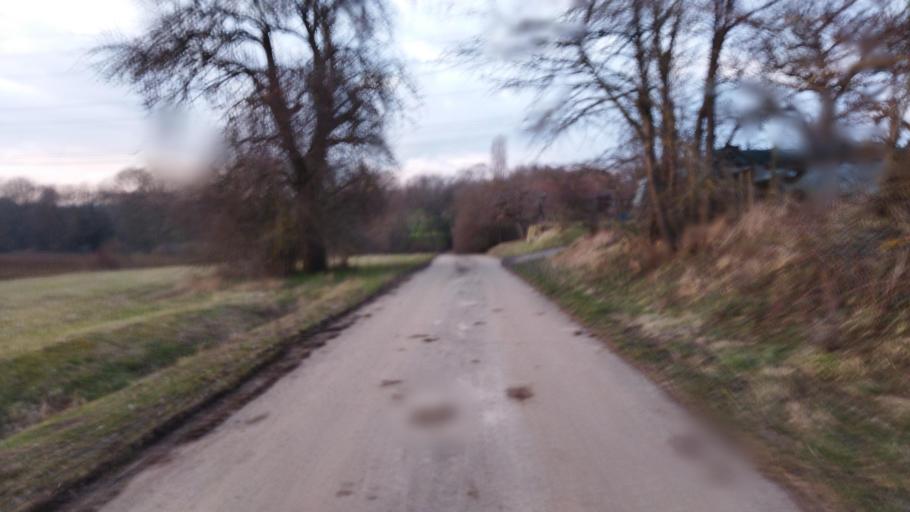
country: DE
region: Baden-Wuerttemberg
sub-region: Regierungsbezirk Stuttgart
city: Neckarwestheim
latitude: 49.0288
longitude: 9.1952
